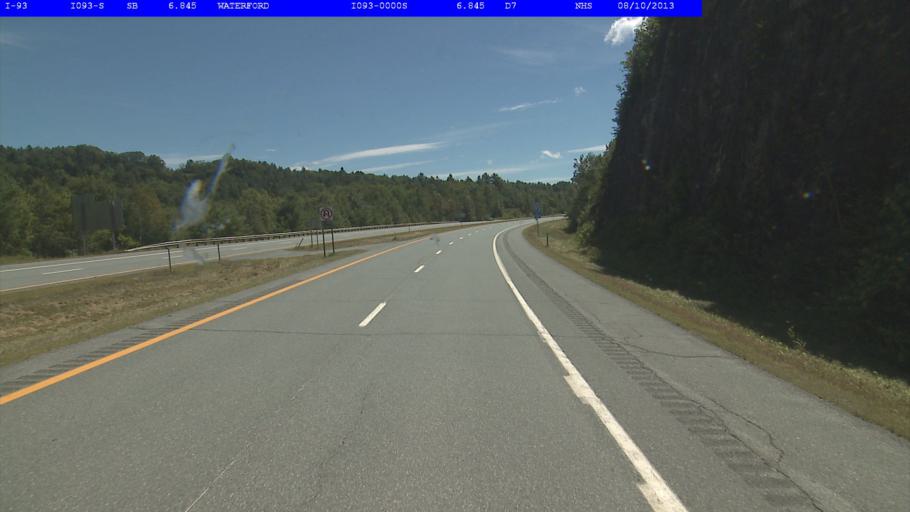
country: US
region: Vermont
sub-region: Caledonia County
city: St Johnsbury
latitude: 44.4274
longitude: -71.9433
